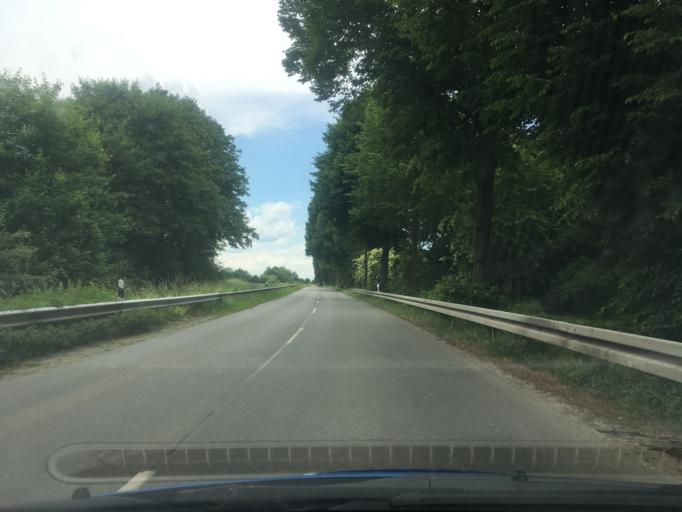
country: DE
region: Lower Saxony
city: Einbeck
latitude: 51.8207
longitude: 9.8447
